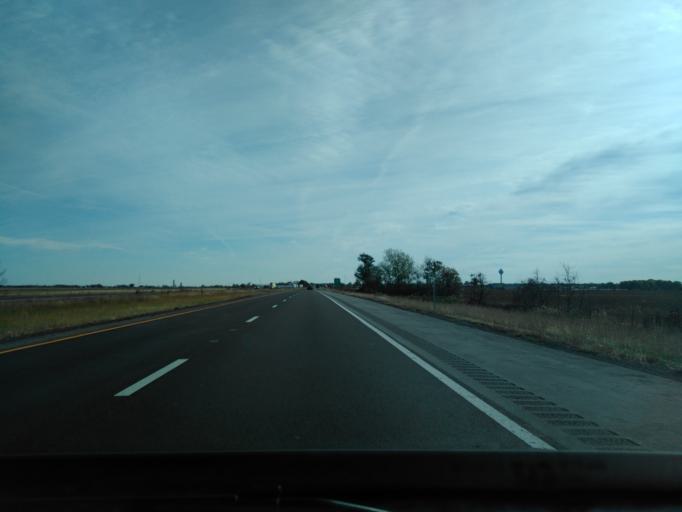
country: US
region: Illinois
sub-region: Madison County
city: Highland
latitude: 38.7864
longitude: -89.6483
